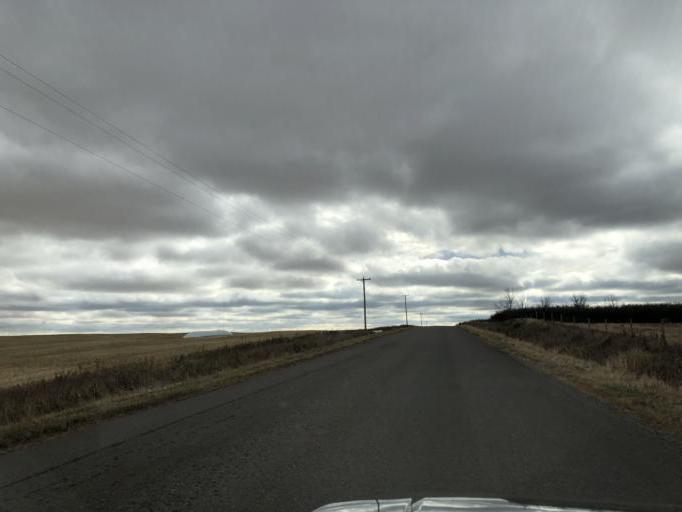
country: CA
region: Alberta
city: Chestermere
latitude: 50.9141
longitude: -113.8829
